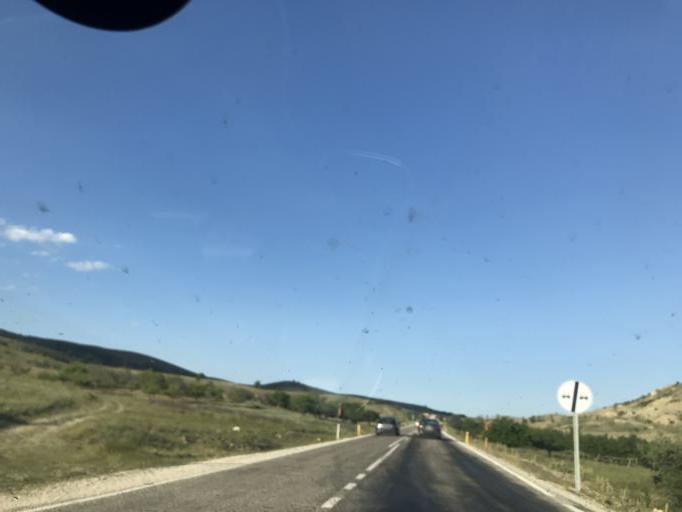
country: TR
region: Antalya
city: Kizilcadag
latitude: 37.1807
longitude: 29.9828
